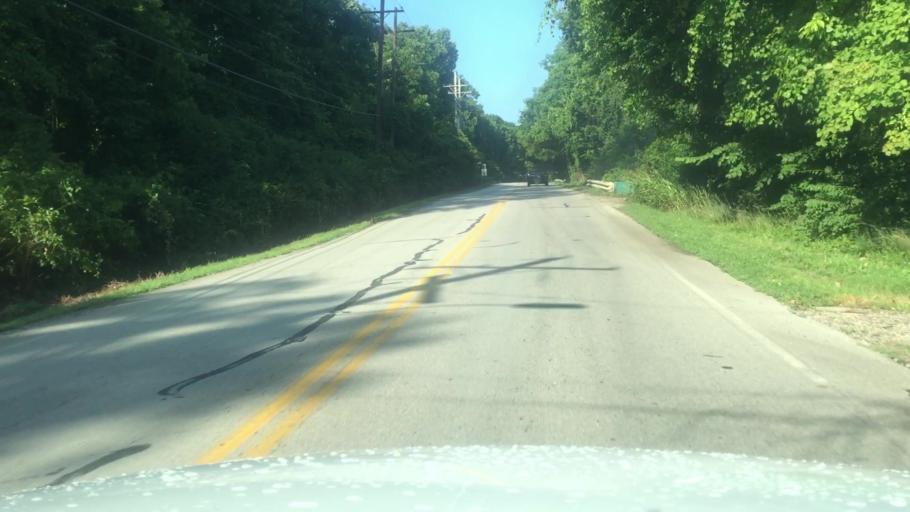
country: US
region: Kansas
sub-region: Wyandotte County
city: Edwardsville
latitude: 39.0474
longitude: -94.7773
